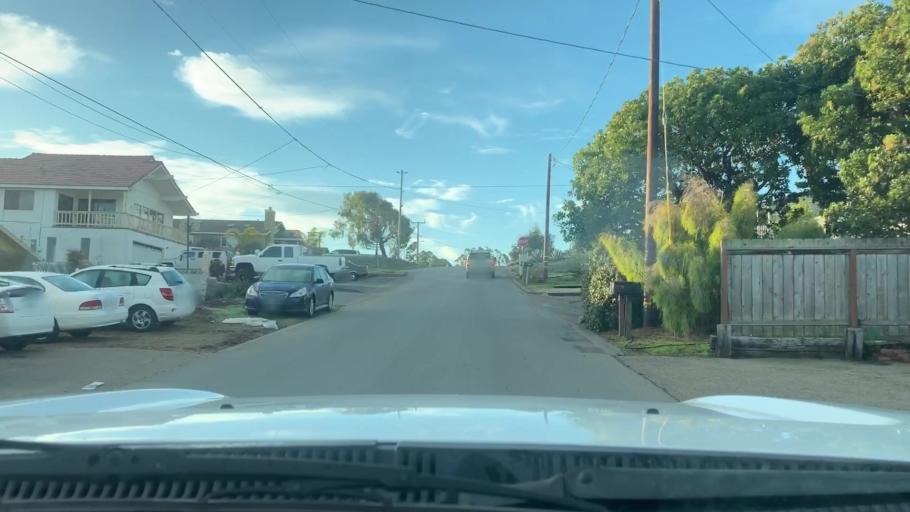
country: US
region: California
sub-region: San Luis Obispo County
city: Los Osos
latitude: 35.3231
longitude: -120.8255
